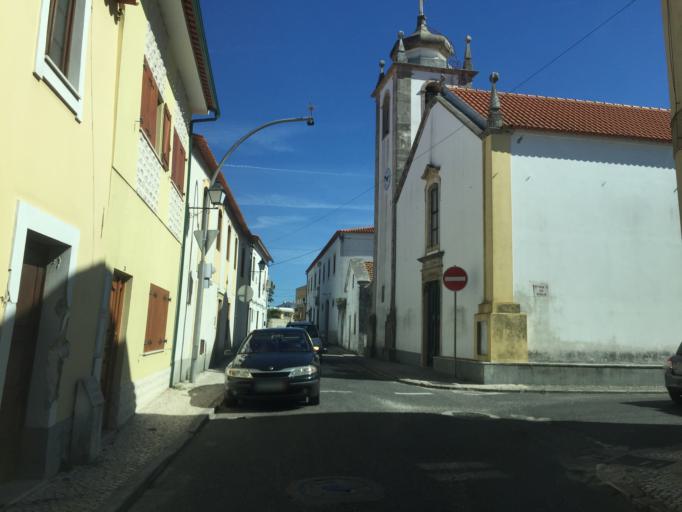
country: PT
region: Coimbra
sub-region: Figueira da Foz
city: Tavarede
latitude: 40.2145
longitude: -8.8519
